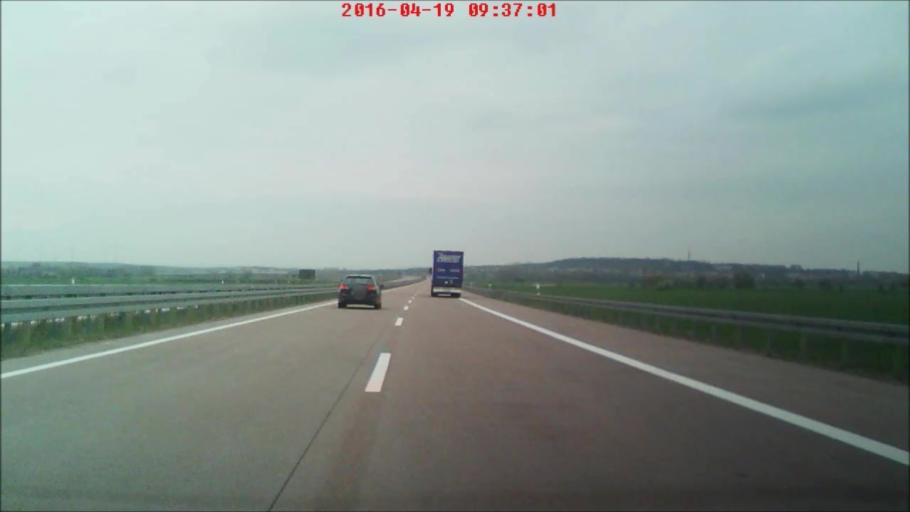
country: DE
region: Thuringia
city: Reinsdorf
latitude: 51.3435
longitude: 11.2604
